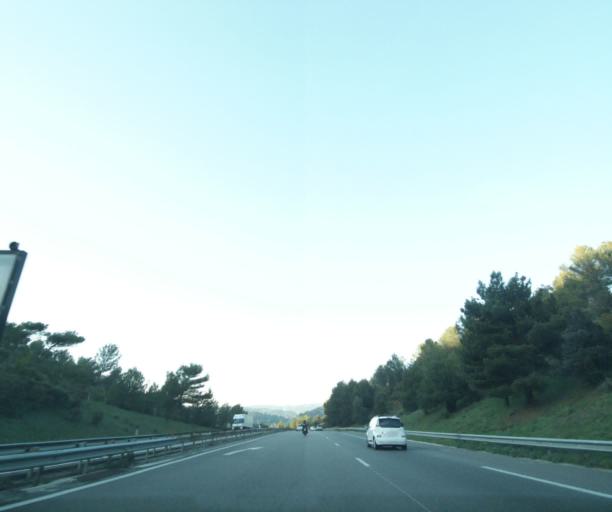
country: FR
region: Provence-Alpes-Cote d'Azur
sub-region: Departement des Bouches-du-Rhone
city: Roquevaire
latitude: 43.3550
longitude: 5.6204
